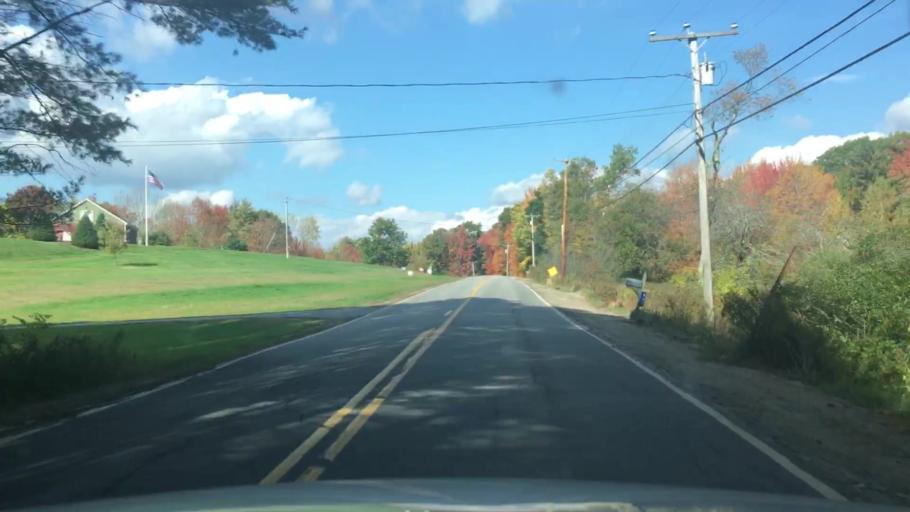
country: US
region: Maine
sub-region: Knox County
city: Warren
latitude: 44.1450
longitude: -69.2345
